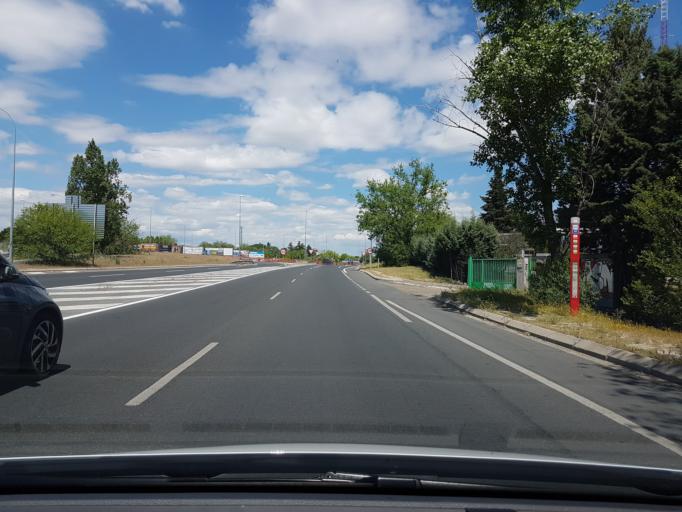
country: ES
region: Madrid
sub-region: Provincia de Madrid
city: Pozuelo de Alarcon
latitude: 40.4278
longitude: -3.8096
